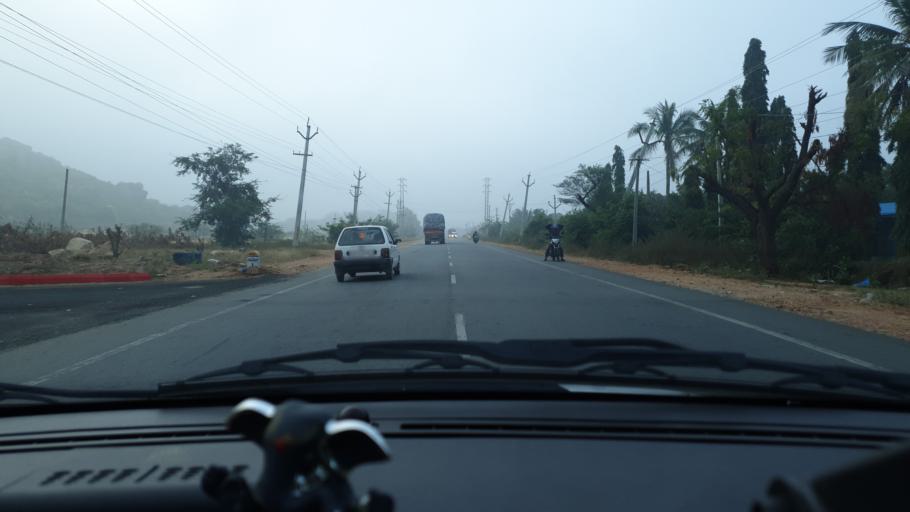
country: IN
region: Telangana
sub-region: Mahbubnagar
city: Farrukhnagar
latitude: 16.8672
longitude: 78.5291
